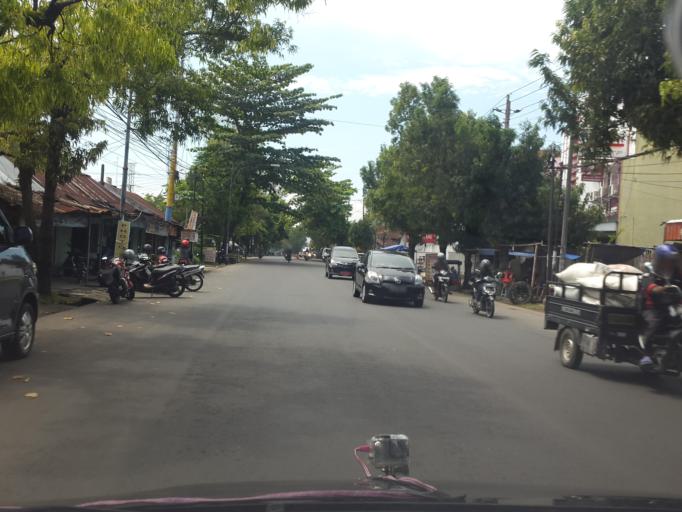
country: ID
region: Central Java
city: Purwokerto
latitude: -7.4302
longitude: 109.2557
